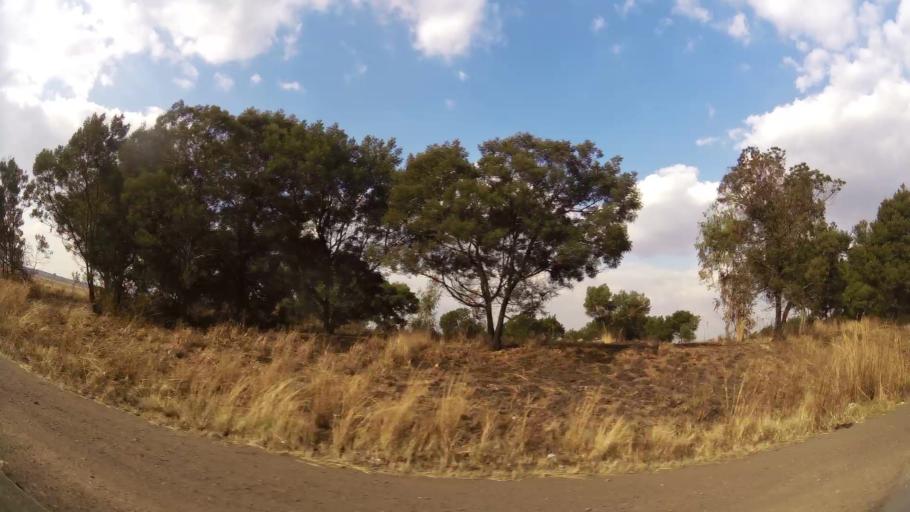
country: ZA
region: Mpumalanga
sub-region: Nkangala District Municipality
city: Delmas
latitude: -26.1693
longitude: 28.6970
